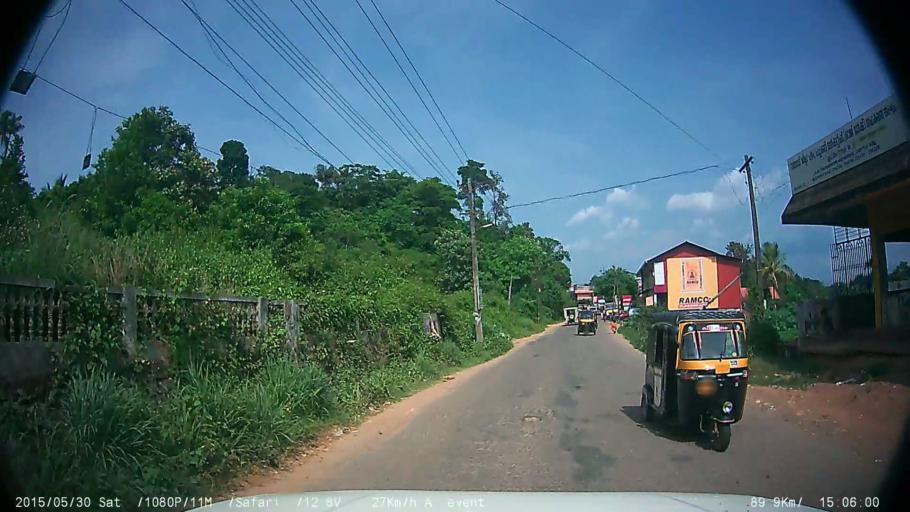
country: IN
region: Kerala
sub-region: Wayanad
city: Panamaram
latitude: 11.8030
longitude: 76.0083
